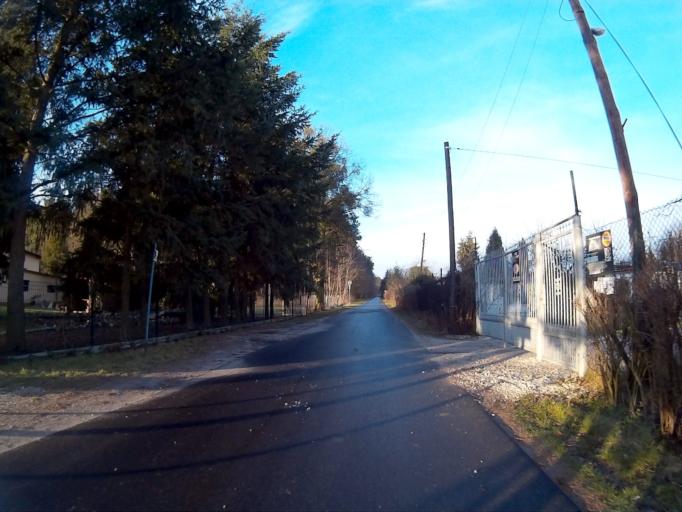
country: PL
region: Kujawsko-Pomorskie
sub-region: Powiat bydgoski
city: Osielsko
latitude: 53.1599
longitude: 18.0439
